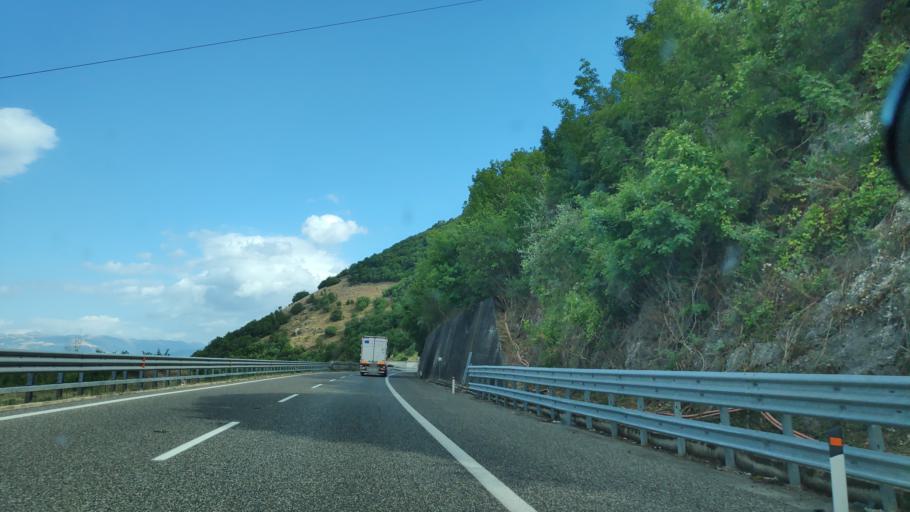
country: IT
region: Campania
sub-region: Provincia di Salerno
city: Sicignano degli Alburni
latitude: 40.5850
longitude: 15.3397
